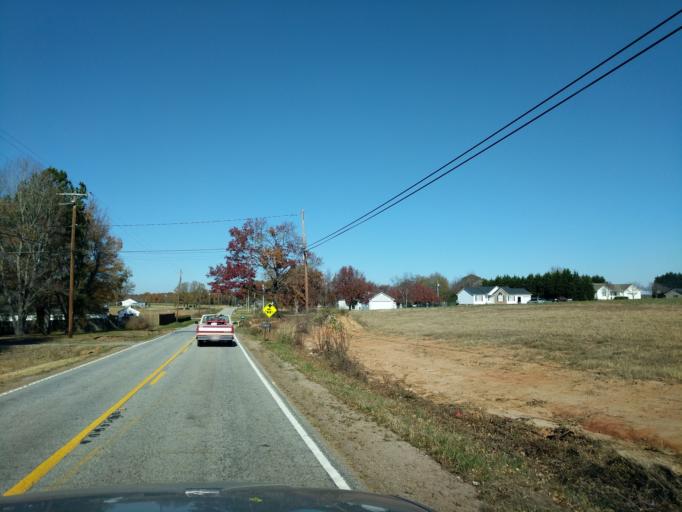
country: US
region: South Carolina
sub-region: Spartanburg County
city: Inman Mills
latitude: 35.0167
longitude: -82.1829
